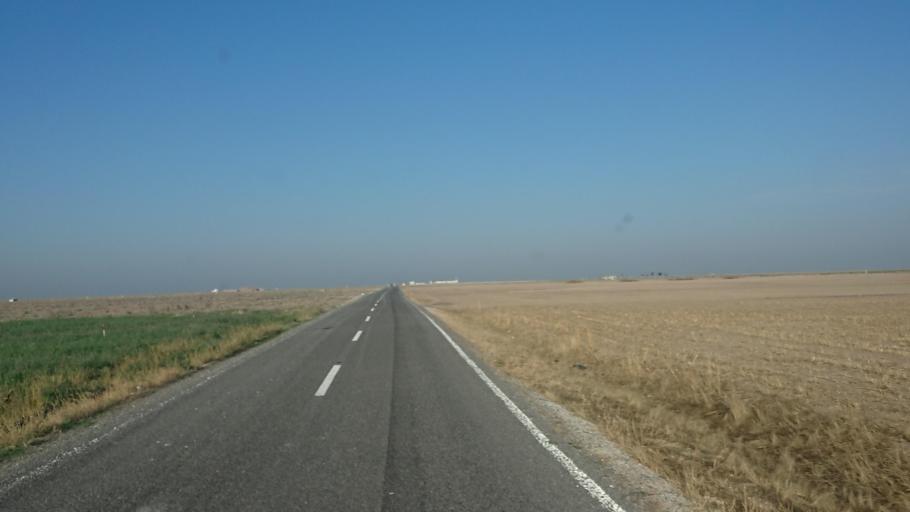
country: TR
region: Aksaray
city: Yesilova
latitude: 38.3879
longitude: 33.7624
